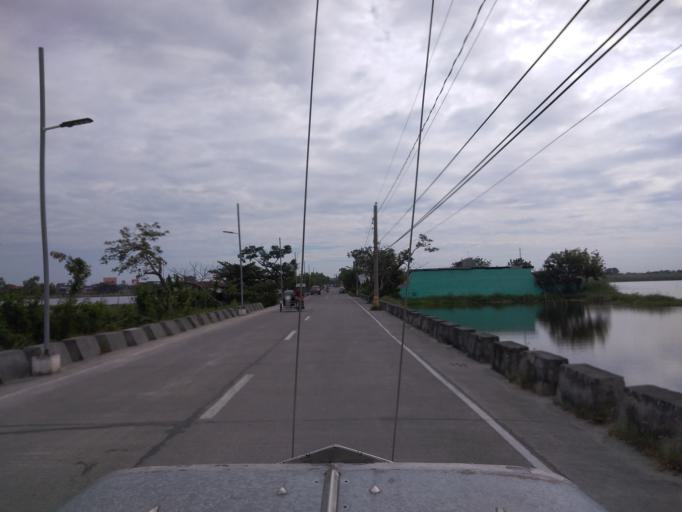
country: PH
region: Central Luzon
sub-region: Province of Pampanga
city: Sexmoan
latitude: 14.9372
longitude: 120.6166
